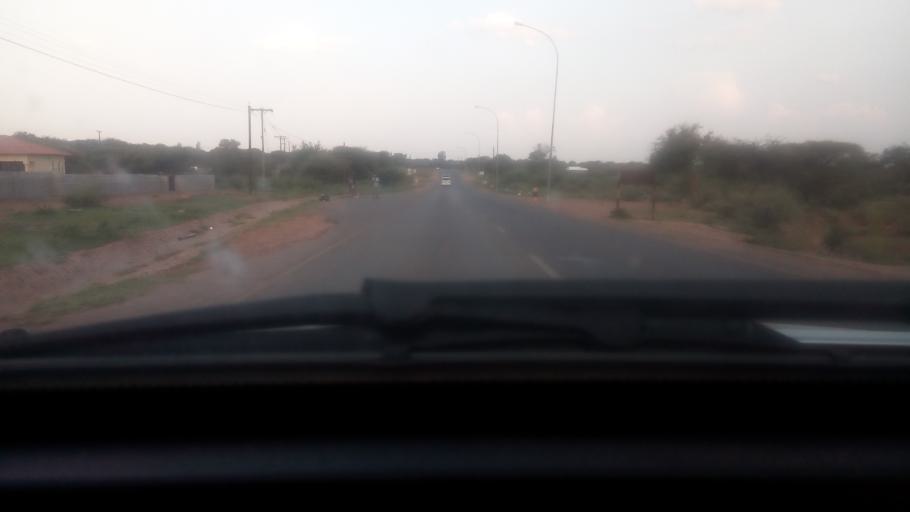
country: BW
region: Kgatleng
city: Bokaa
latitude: -24.4335
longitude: 26.0325
